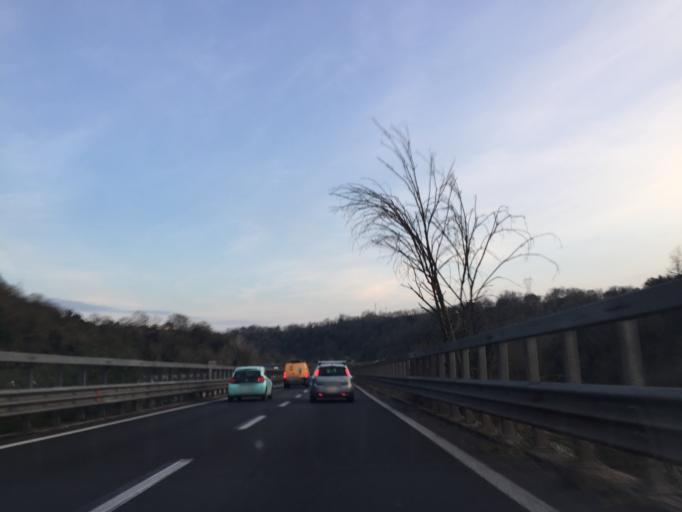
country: IT
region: Latium
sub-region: Citta metropolitana di Roma Capitale
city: Monte Caminetto
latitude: 42.0109
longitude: 12.4377
